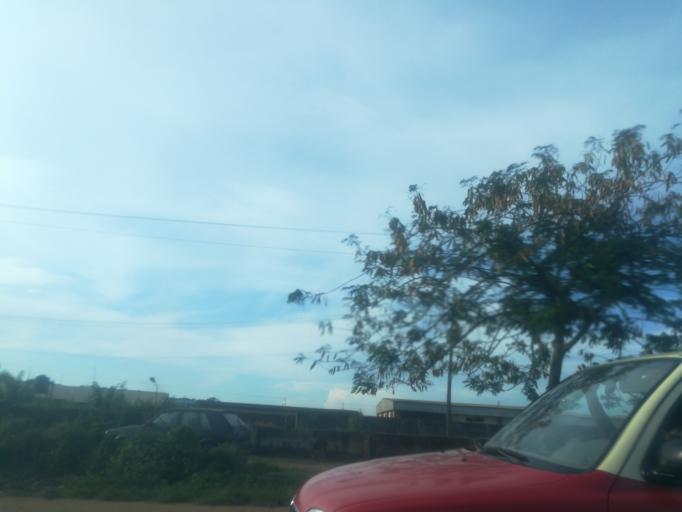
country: NG
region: Oyo
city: Ibadan
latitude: 7.3370
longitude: 3.8931
